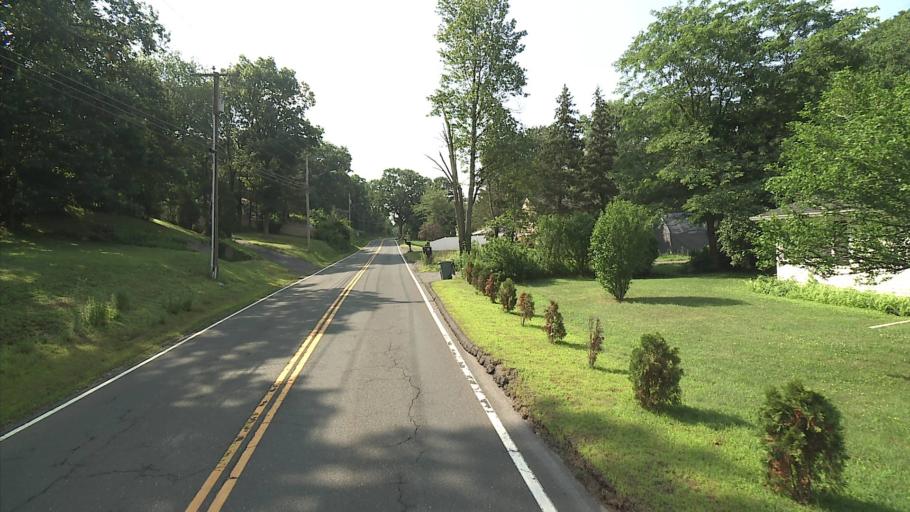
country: US
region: Connecticut
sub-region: New Haven County
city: Wolcott
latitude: 41.5949
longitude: -72.9591
